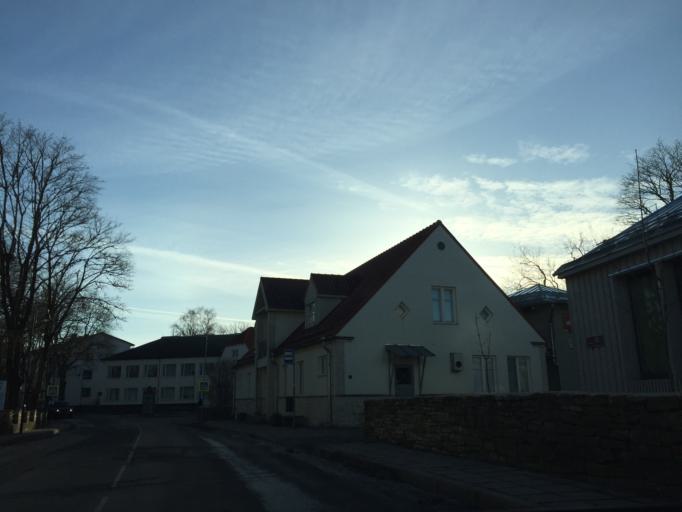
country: EE
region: Saare
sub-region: Kuressaare linn
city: Kuressaare
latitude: 58.2527
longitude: 22.4799
